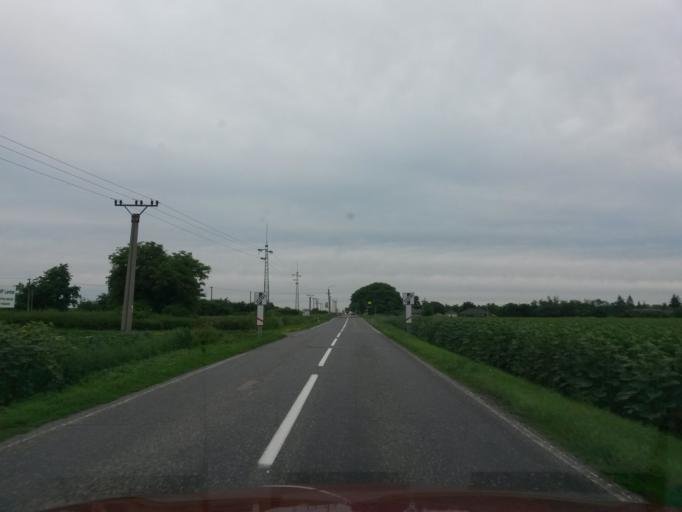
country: SK
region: Nitriansky
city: Levice
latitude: 48.1608
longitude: 18.5557
